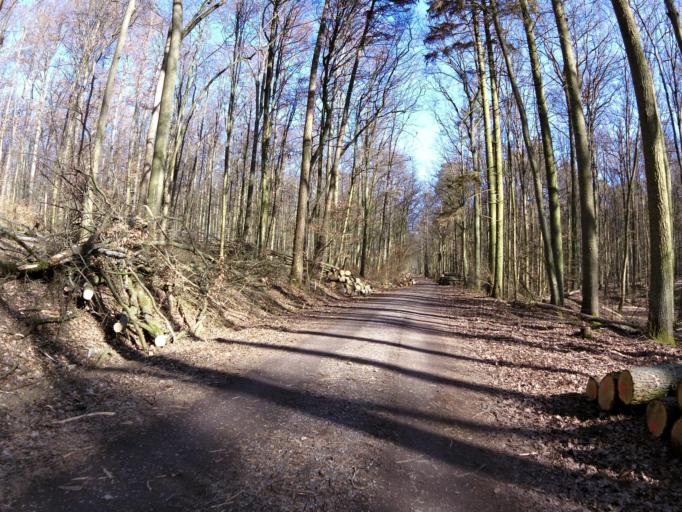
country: DE
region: Bavaria
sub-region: Regierungsbezirk Unterfranken
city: Rimpar
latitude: 49.8554
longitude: 9.9860
